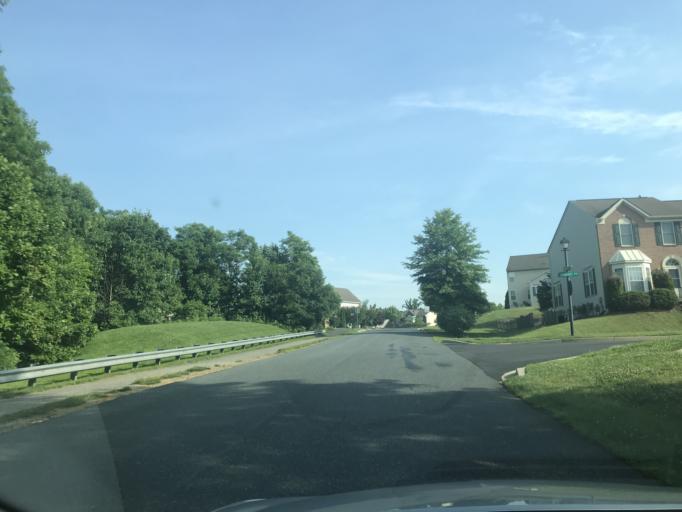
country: US
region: Maryland
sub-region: Harford County
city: Bel Air North
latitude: 39.5542
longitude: -76.3602
